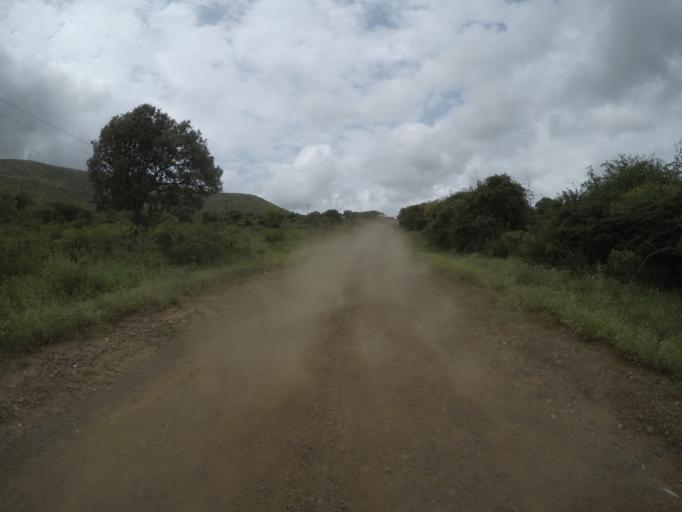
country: ZA
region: KwaZulu-Natal
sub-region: uThungulu District Municipality
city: Empangeni
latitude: -28.5995
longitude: 31.8933
